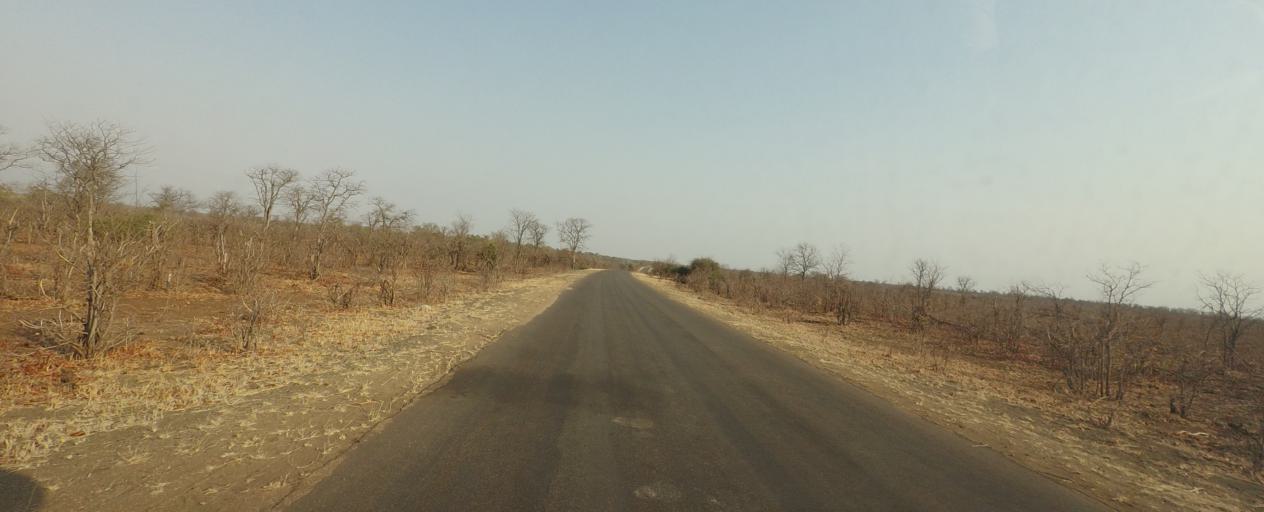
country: ZA
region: Limpopo
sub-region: Mopani District Municipality
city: Giyani
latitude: -23.0735
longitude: 31.4082
